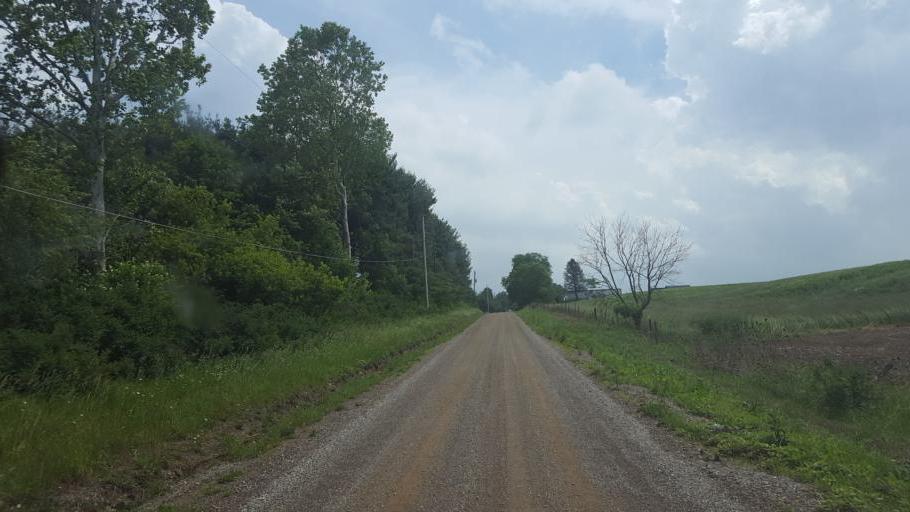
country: US
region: Ohio
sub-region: Knox County
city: Oak Hill
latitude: 40.2892
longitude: -82.2688
